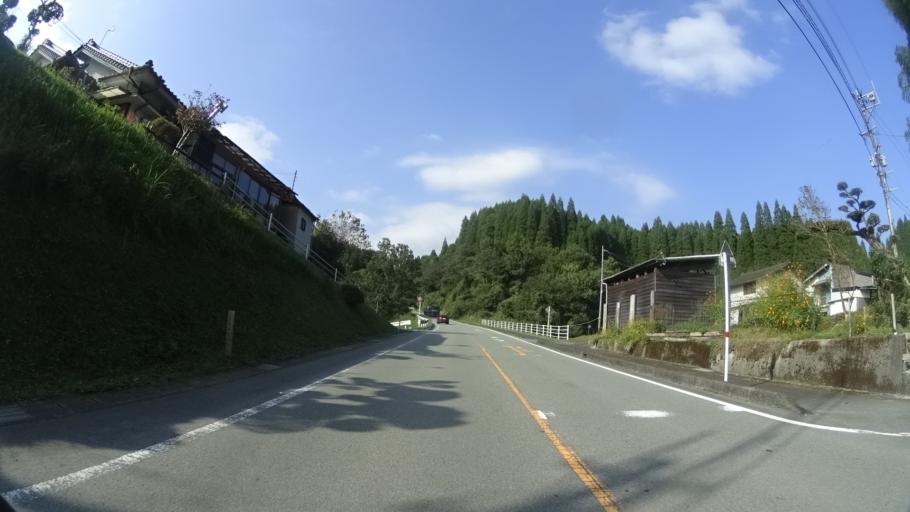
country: JP
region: Oita
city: Tsukawaki
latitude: 33.1312
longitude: 131.0876
